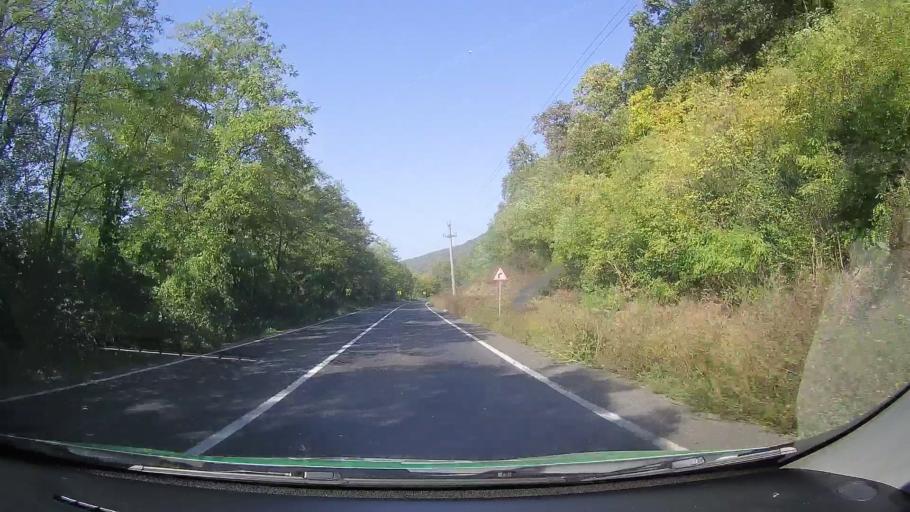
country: RO
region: Arad
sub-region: Comuna Savarsin
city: Savarsin
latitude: 46.0033
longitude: 22.2775
